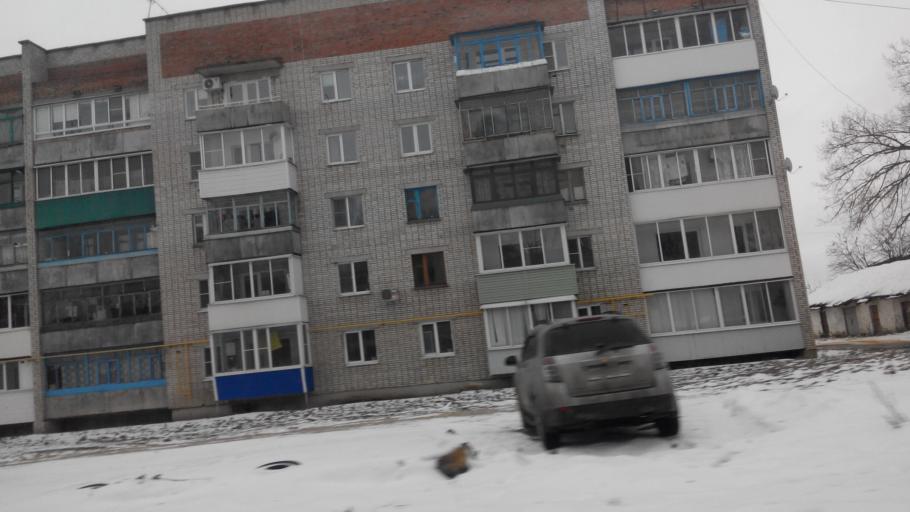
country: RU
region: Tula
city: Uzlovaya
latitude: 53.9832
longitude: 38.1912
